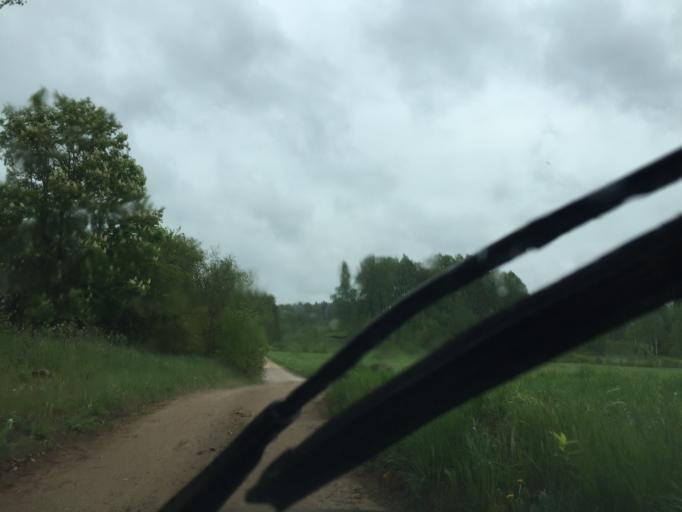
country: LV
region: Kegums
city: Kegums
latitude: 56.7354
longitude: 24.7439
